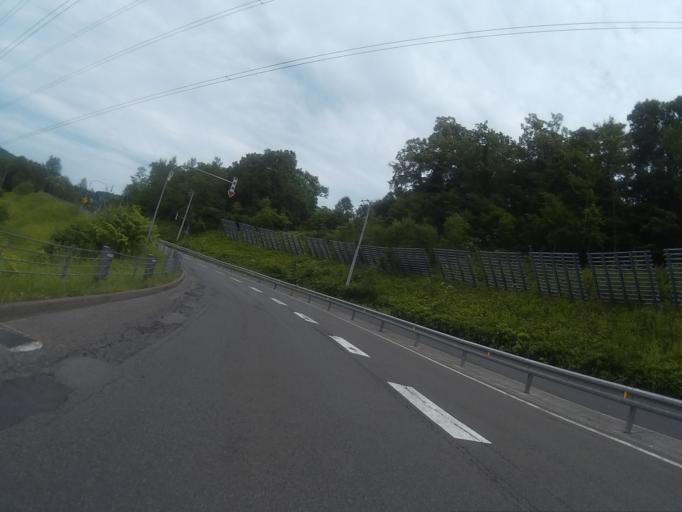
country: JP
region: Hokkaido
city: Otaru
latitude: 42.8523
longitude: 141.0719
